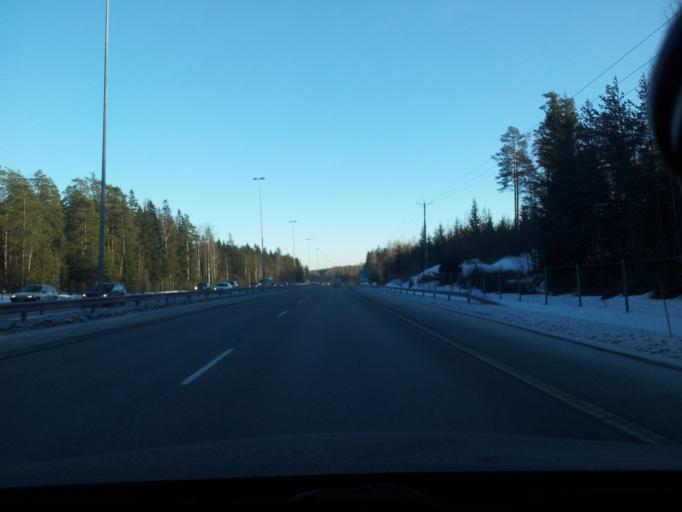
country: FI
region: Uusimaa
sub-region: Helsinki
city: Espoo
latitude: 60.2515
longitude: 24.5320
